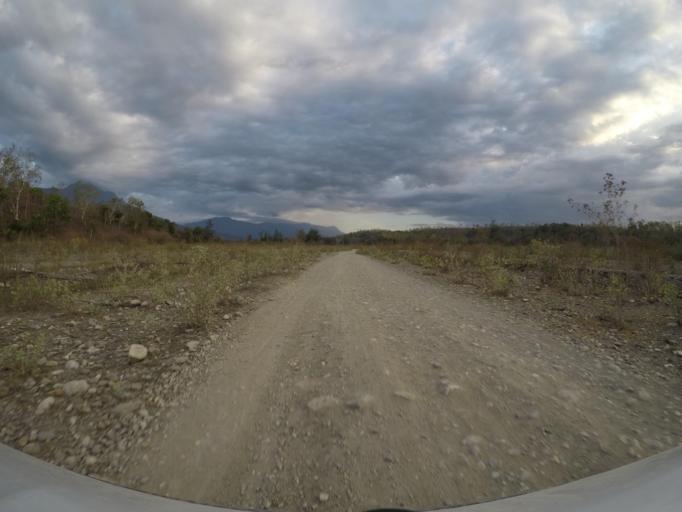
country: TL
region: Bobonaro
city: Maliana
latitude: -8.8984
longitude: 125.2091
